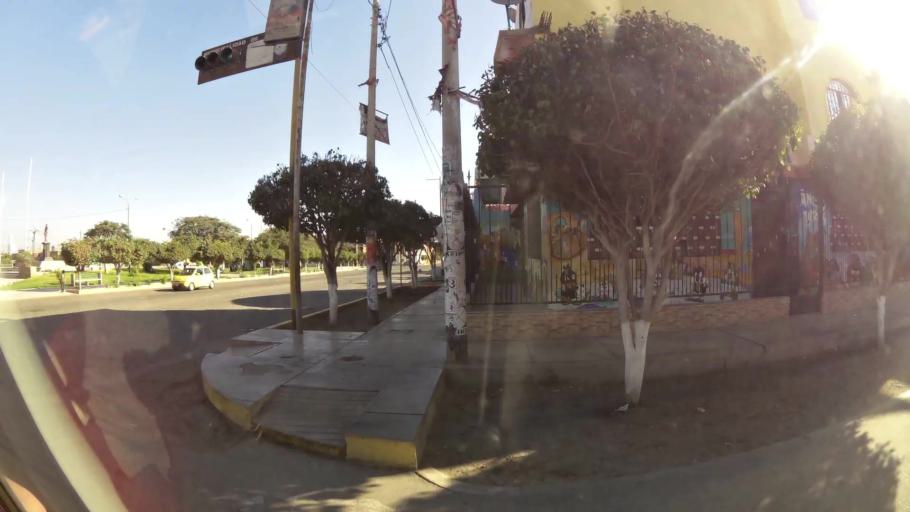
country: PE
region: Ica
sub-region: Provincia de Ica
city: La Tinguina
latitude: -14.0462
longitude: -75.6987
